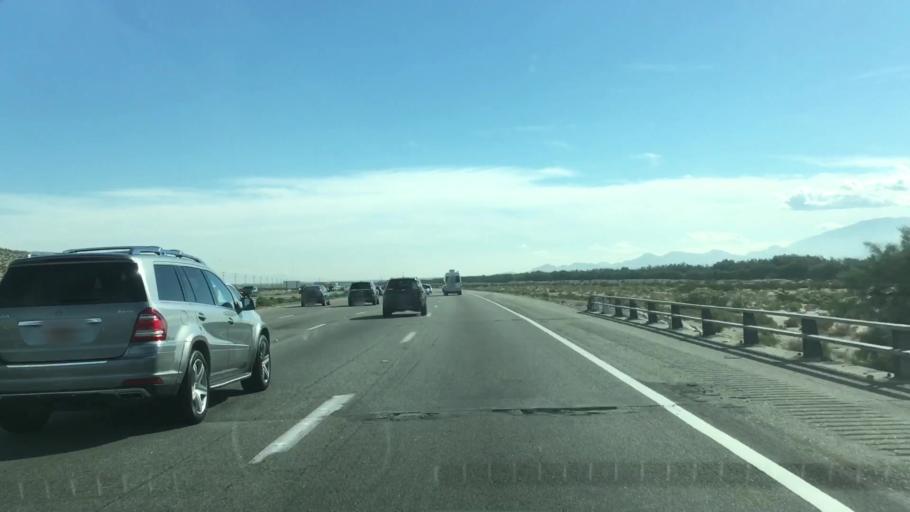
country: US
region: California
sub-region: Riverside County
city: Garnet
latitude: 33.8689
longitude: -116.4915
